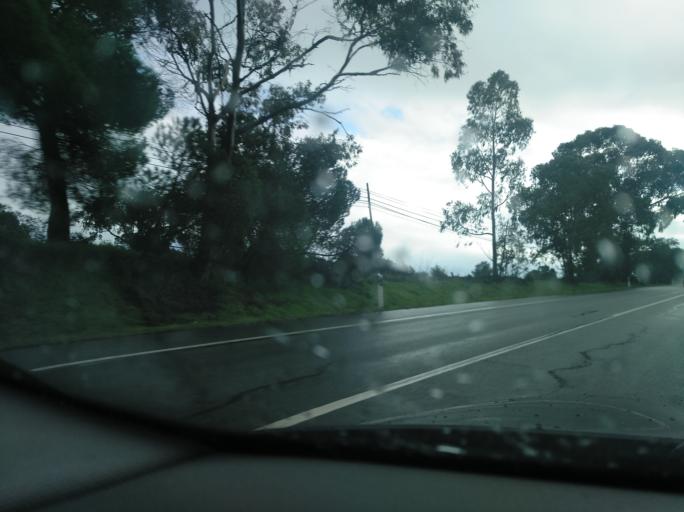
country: PT
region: Setubal
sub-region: Grandola
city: Grandola
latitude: 38.1041
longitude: -8.4183
